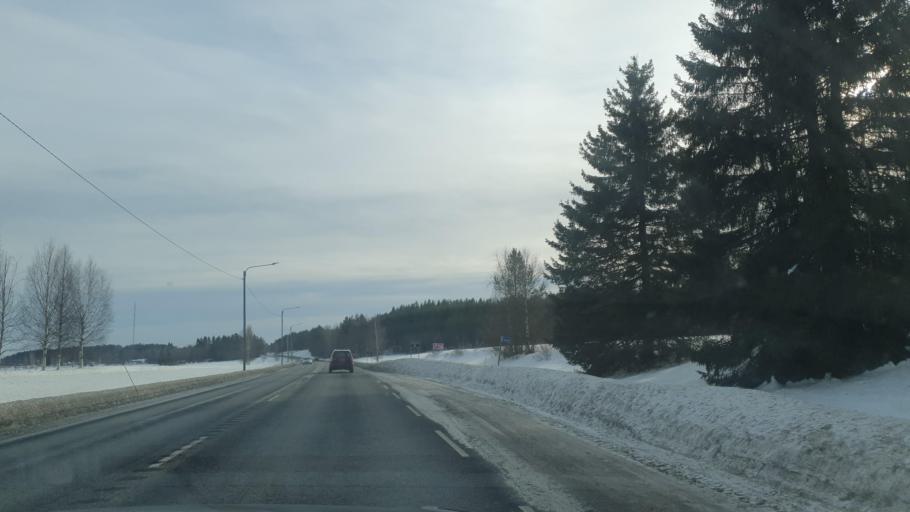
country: FI
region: Northern Ostrobothnia
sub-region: Oulu
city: Muhos
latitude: 64.8445
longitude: 25.9014
